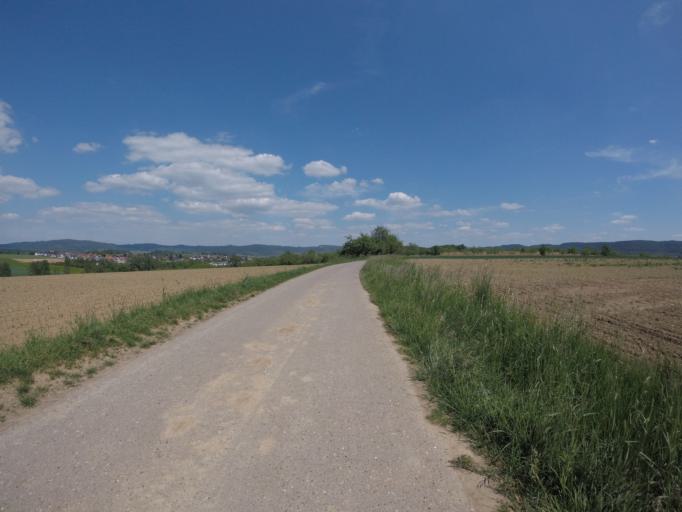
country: DE
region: Baden-Wuerttemberg
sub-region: Regierungsbezirk Stuttgart
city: Allmersbach im Tal
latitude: 48.9225
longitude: 9.4612
